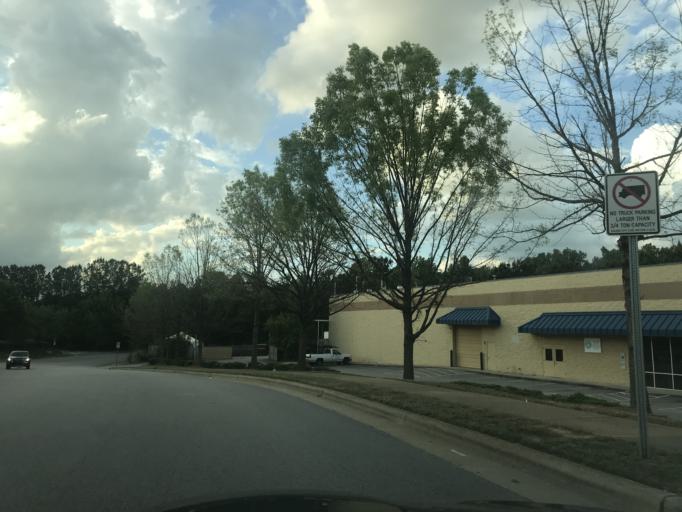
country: US
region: North Carolina
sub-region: Wake County
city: Raleigh
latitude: 35.8378
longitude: -78.6064
